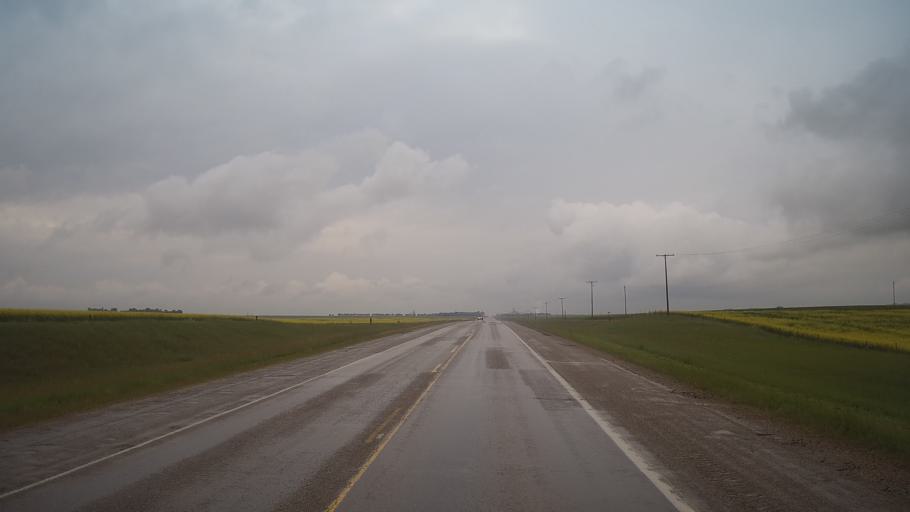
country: CA
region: Saskatchewan
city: Unity
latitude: 52.4350
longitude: -109.0467
